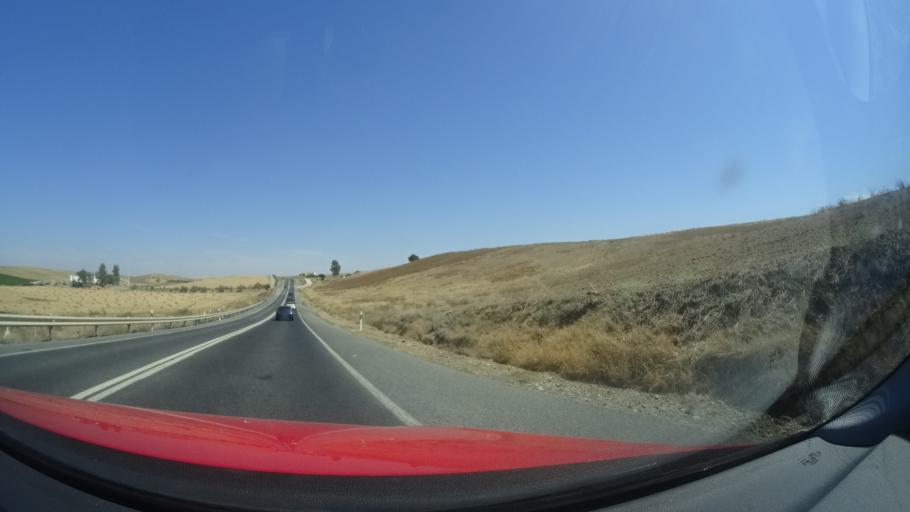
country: ES
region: Andalusia
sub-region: Provincia de Sevilla
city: Las Cabezas de San Juan
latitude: 36.9565
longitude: -5.8948
